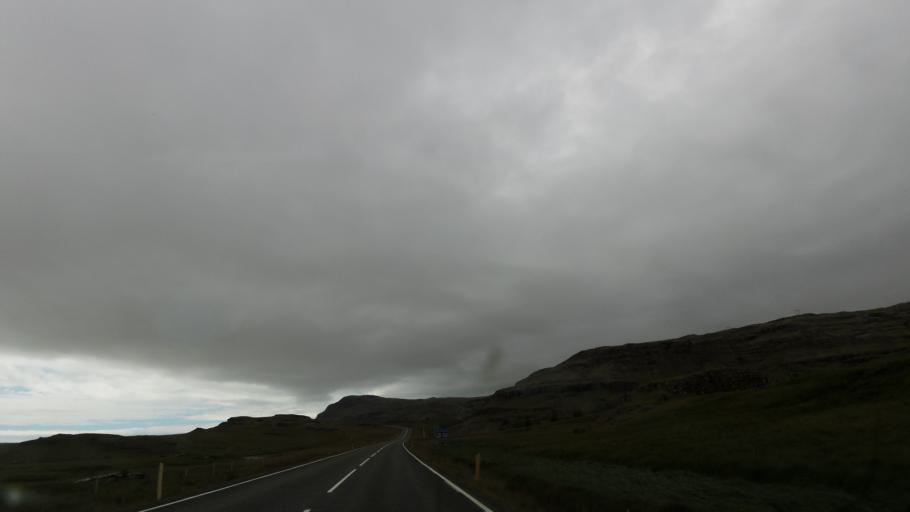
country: IS
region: East
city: Hoefn
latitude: 64.2168
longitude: -15.7085
